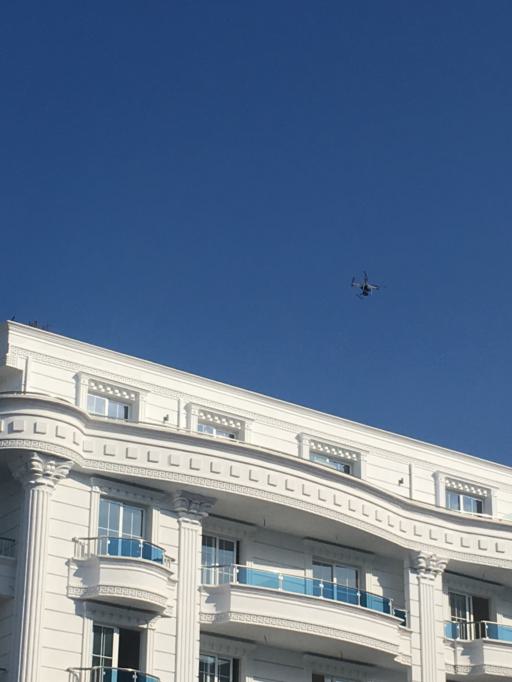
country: AL
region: Tirane
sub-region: Rrethi i Kavajes
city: Golem
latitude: 41.2640
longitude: 19.5195
